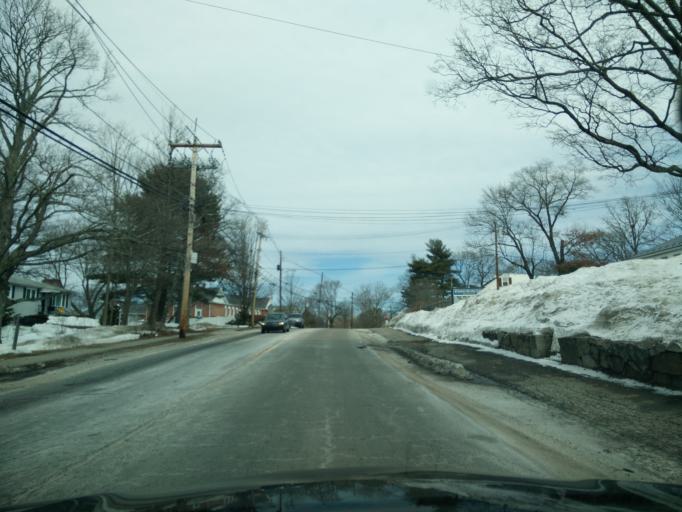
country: US
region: Massachusetts
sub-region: Norfolk County
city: Walpole
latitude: 42.1608
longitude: -71.2396
